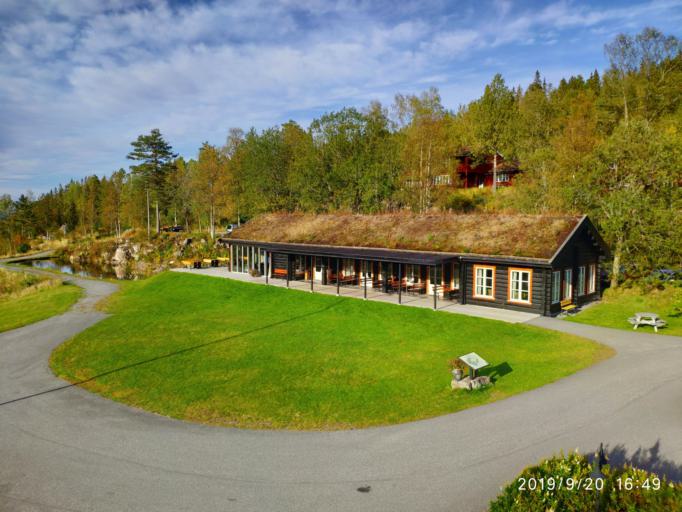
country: NO
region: Buskerud
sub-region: Hole
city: Vik
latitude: 60.0470
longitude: 10.3215
